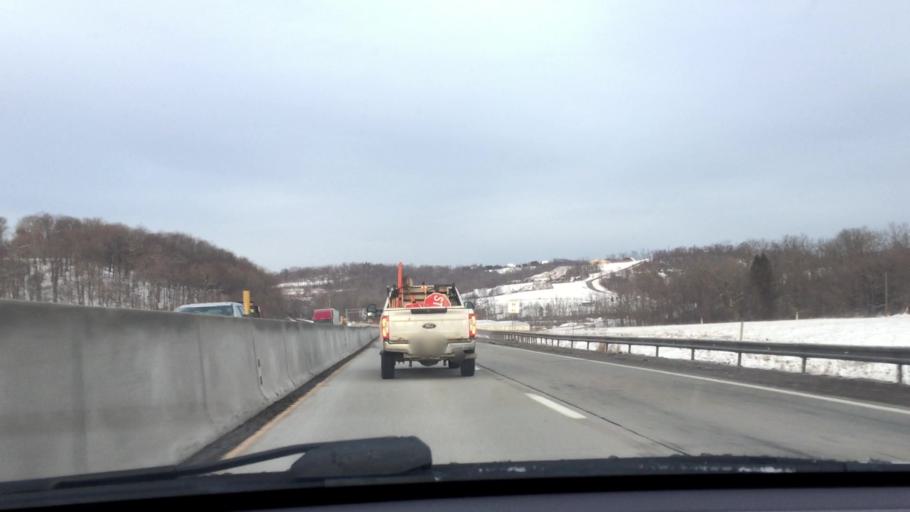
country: US
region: Pennsylvania
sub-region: Washington County
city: East Washington
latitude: 40.1662
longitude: -80.1690
